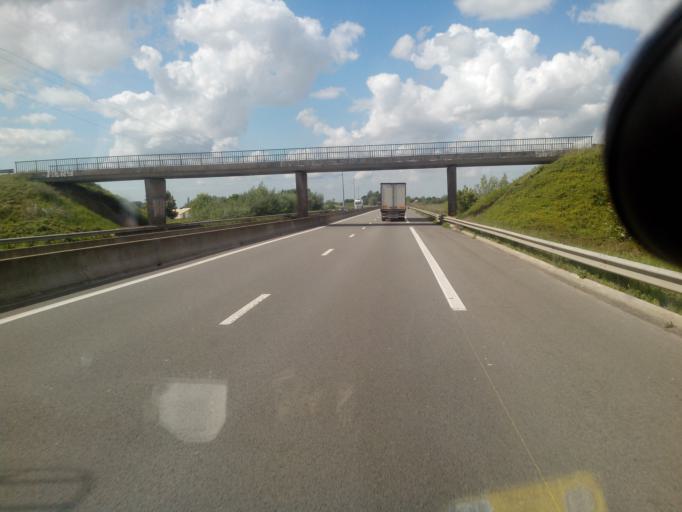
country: FR
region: Nord-Pas-de-Calais
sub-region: Departement du Nord
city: Herzeele
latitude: 50.8785
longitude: 2.5219
